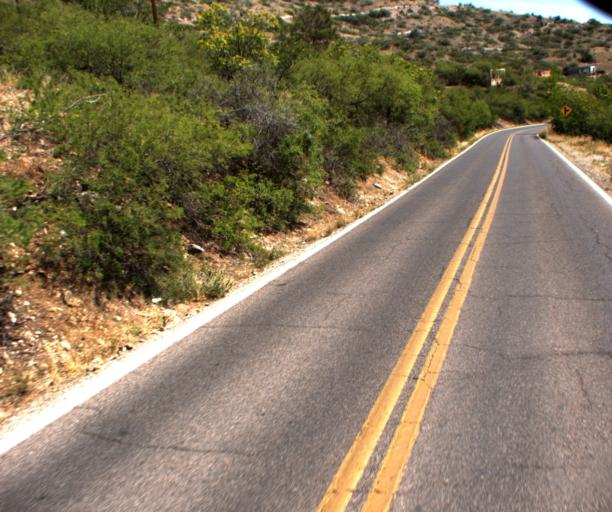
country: US
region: Arizona
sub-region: Yavapai County
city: Clarkdale
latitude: 34.7461
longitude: -112.1087
